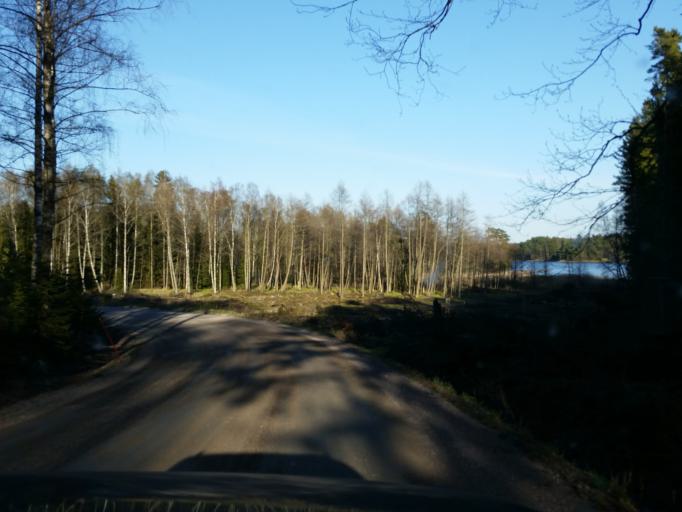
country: FI
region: Uusimaa
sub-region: Helsinki
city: Espoo
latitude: 60.0993
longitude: 24.5851
